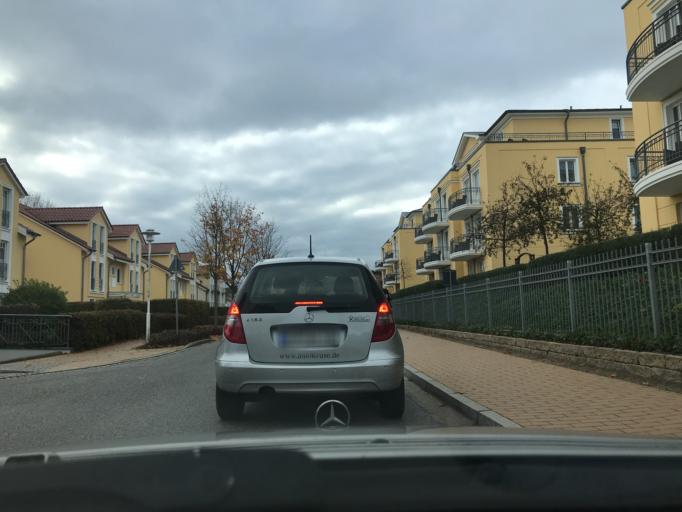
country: DE
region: Mecklenburg-Vorpommern
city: Seebad Bansin
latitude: 53.9702
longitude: 14.1442
